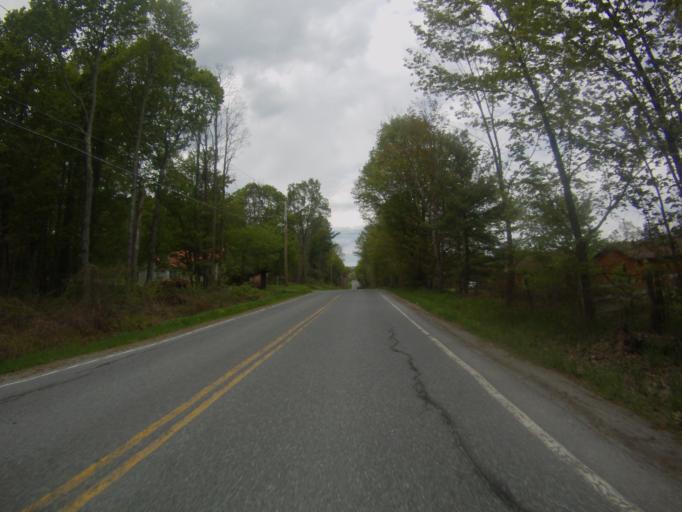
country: US
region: New York
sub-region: Essex County
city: Port Henry
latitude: 44.0268
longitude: -73.5012
